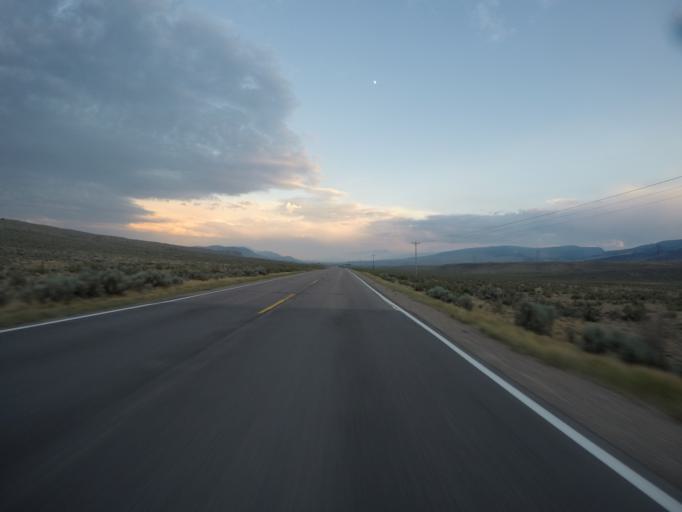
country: US
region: Colorado
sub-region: Grand County
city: Kremmling
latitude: 40.0841
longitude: -106.4159
